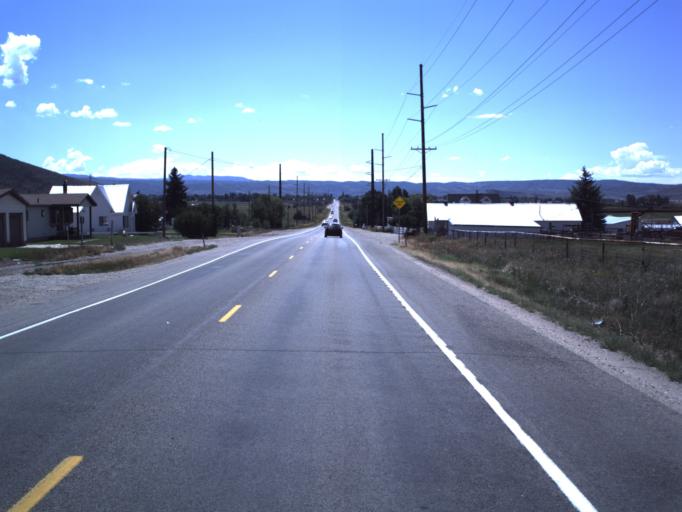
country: US
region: Utah
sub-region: Summit County
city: Kamas
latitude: 40.6712
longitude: -111.2809
